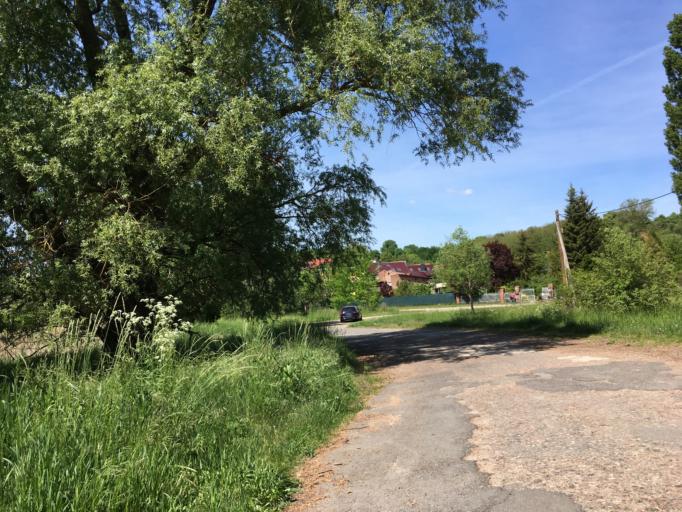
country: DE
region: Brandenburg
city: Liepe
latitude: 52.8597
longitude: 13.9709
